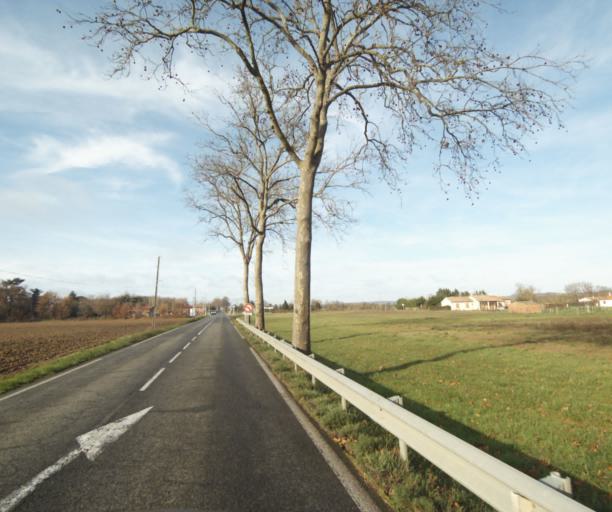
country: FR
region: Midi-Pyrenees
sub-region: Departement du Tarn-et-Garonne
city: Nohic
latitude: 43.8732
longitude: 1.4618
